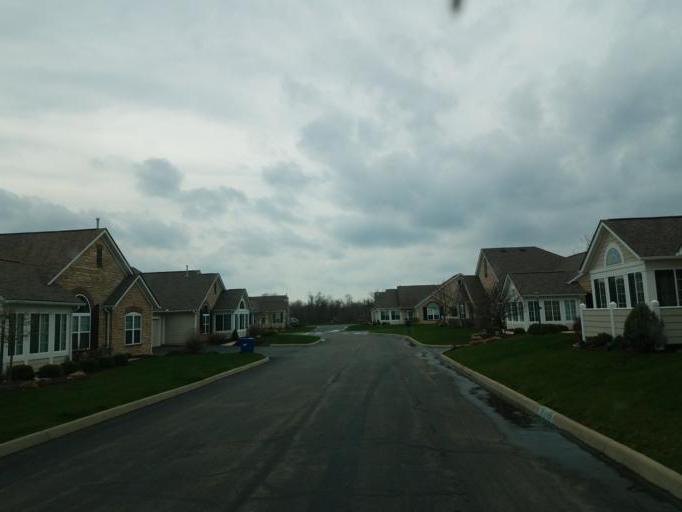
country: US
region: Ohio
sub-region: Richland County
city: Lexington
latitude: 40.7211
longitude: -82.5642
